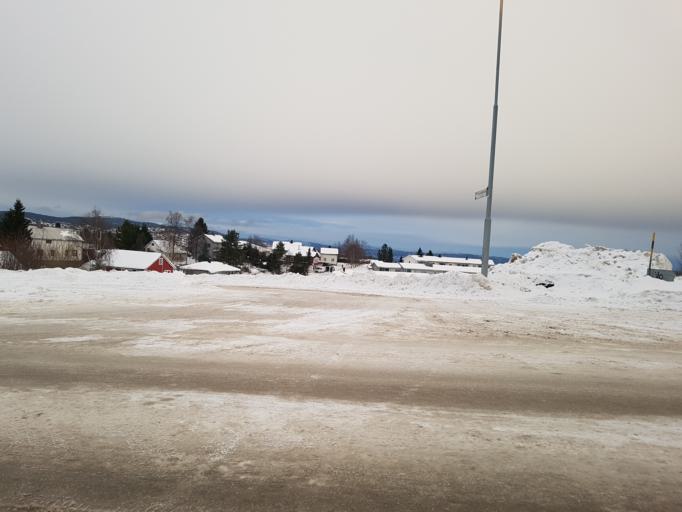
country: NO
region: Sor-Trondelag
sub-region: Trondheim
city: Trondheim
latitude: 63.3672
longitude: 10.3847
